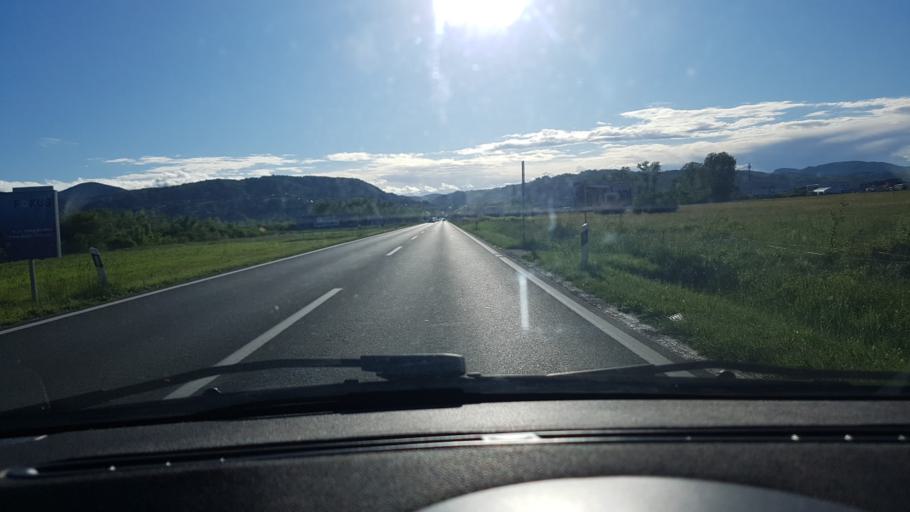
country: HR
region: Zagrebacka
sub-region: Grad Samobor
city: Samobor
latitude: 45.7984
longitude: 15.7435
